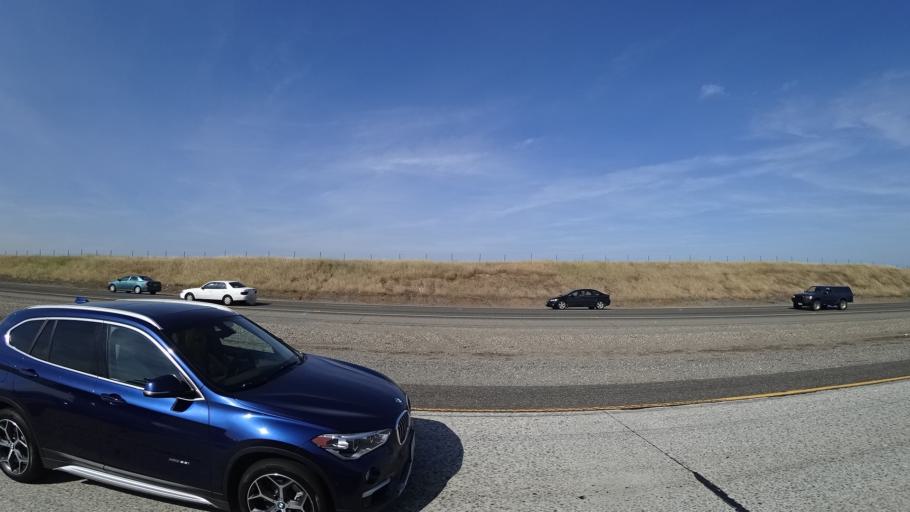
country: US
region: California
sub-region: Butte County
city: Durham
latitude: 39.6682
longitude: -121.7474
